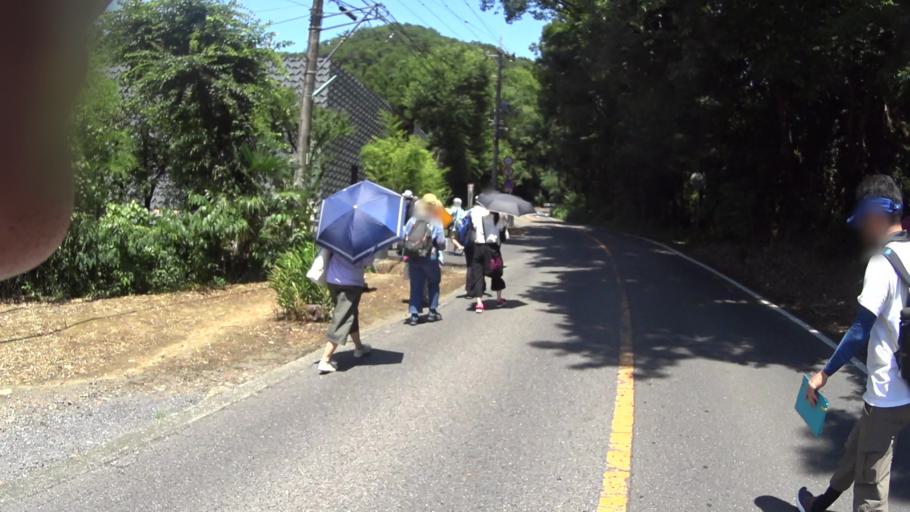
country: JP
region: Gunma
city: Ota
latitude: 36.3124
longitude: 139.3750
